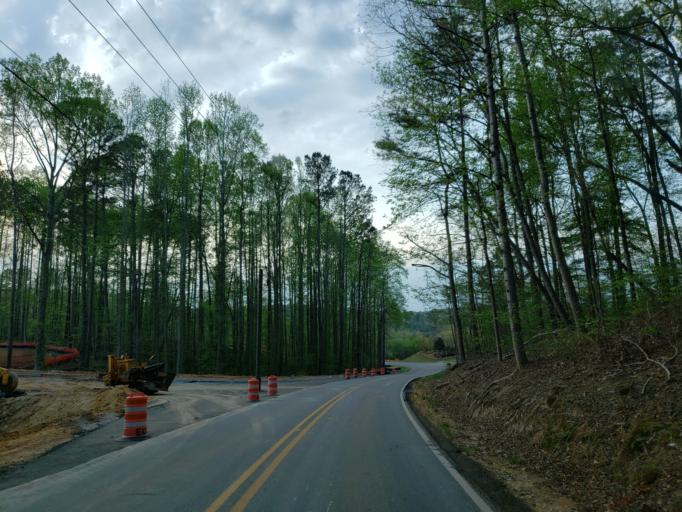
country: US
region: Georgia
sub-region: Cherokee County
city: Canton
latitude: 34.2909
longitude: -84.4595
